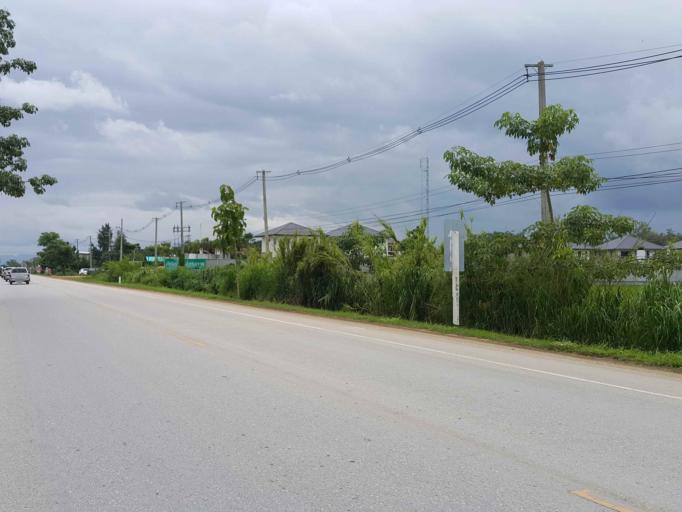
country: TH
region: Chiang Mai
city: San Sai
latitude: 18.8220
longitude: 99.0503
